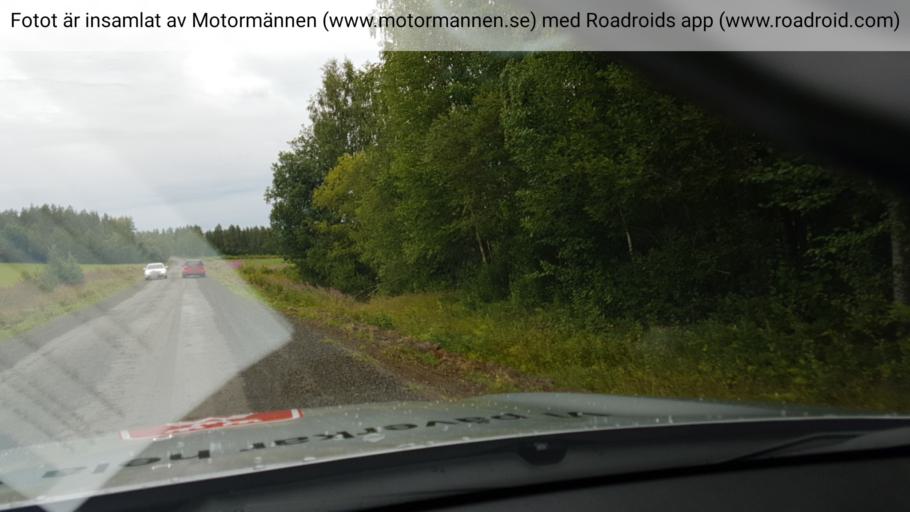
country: SE
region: Norrbotten
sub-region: Alvsbyns Kommun
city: AElvsbyn
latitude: 65.9841
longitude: 21.2101
